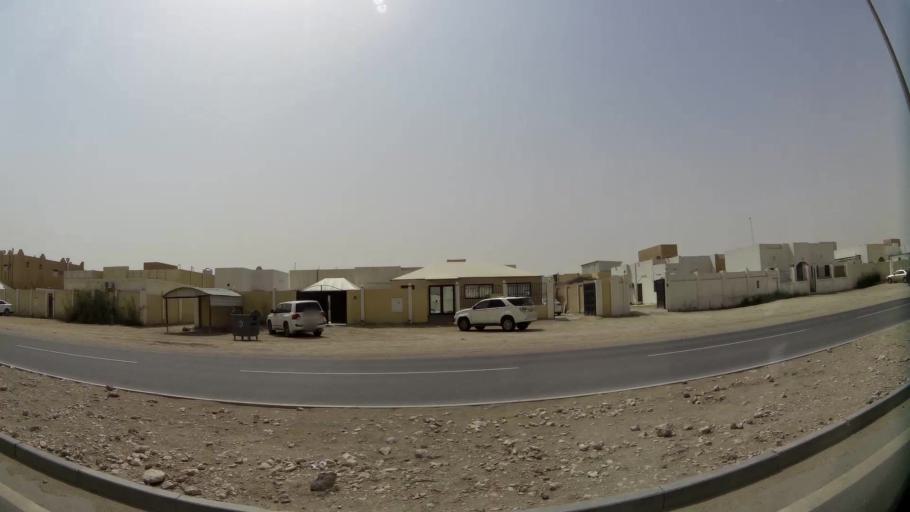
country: QA
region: Baladiyat ar Rayyan
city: Ar Rayyan
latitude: 25.2431
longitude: 51.3793
